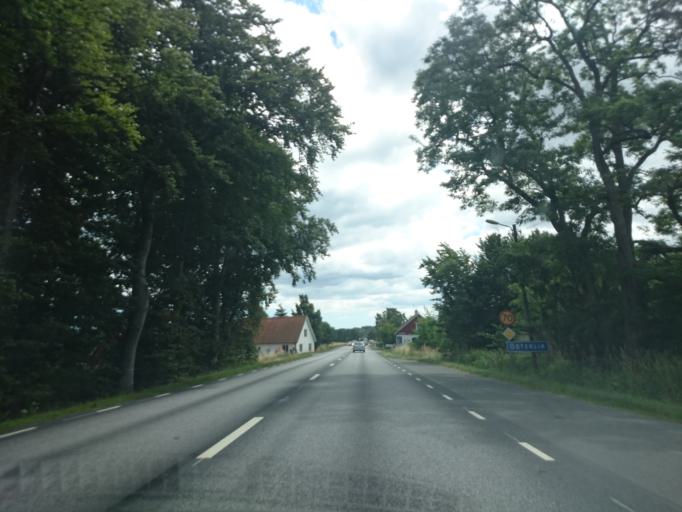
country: SE
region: Skane
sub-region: Kristianstads Kommun
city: Degeberga
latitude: 55.8141
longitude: 14.1340
